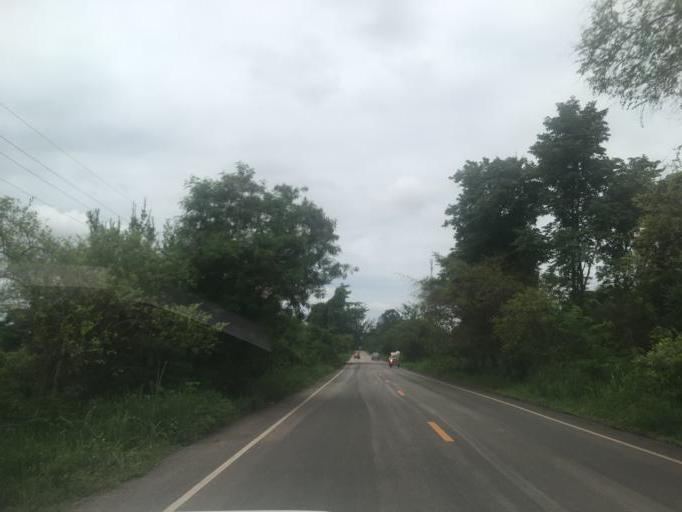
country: TH
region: Changwat Udon Thani
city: Udon Thani
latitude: 17.3258
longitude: 102.7133
